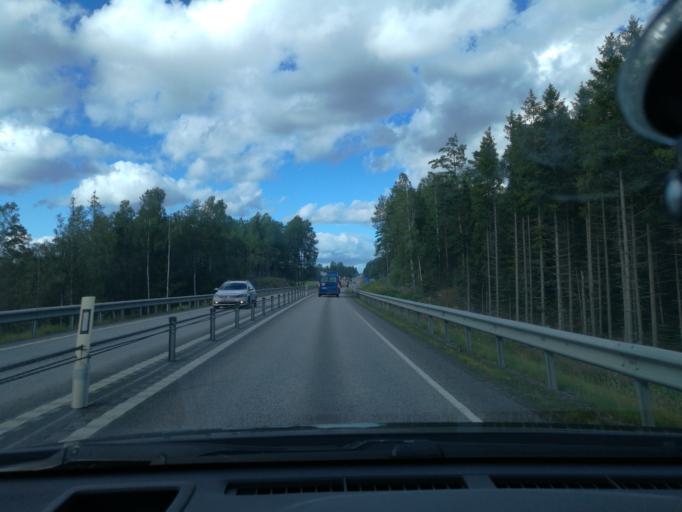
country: SE
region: Kronoberg
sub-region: Vaxjo Kommun
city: Braas
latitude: 57.0301
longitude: 15.0645
